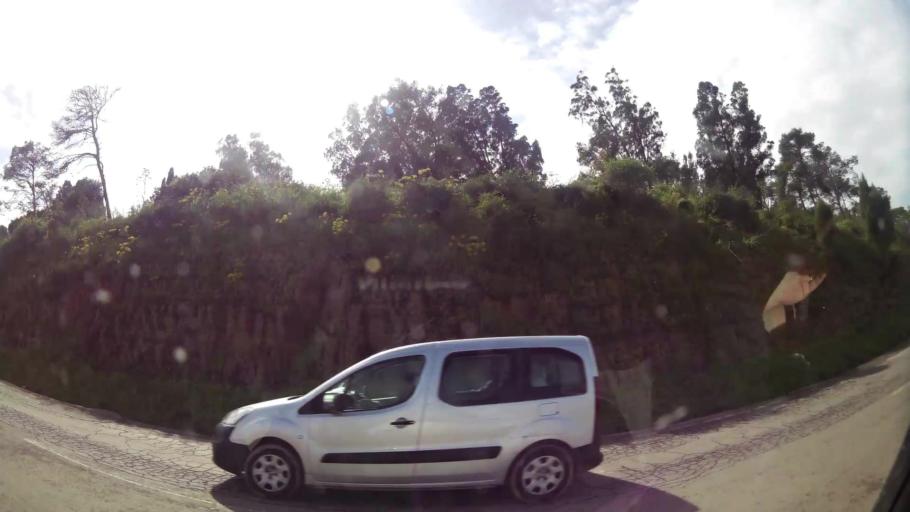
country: MA
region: Grand Casablanca
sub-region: Mohammedia
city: Mohammedia
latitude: 33.6562
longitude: -7.4000
